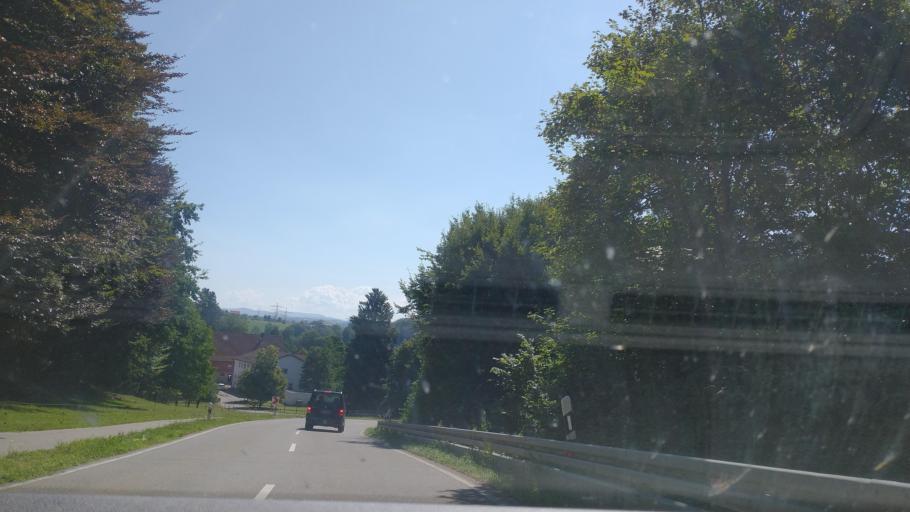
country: DE
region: Bavaria
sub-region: Swabia
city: Hergensweiler
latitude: 47.6550
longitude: 9.7756
